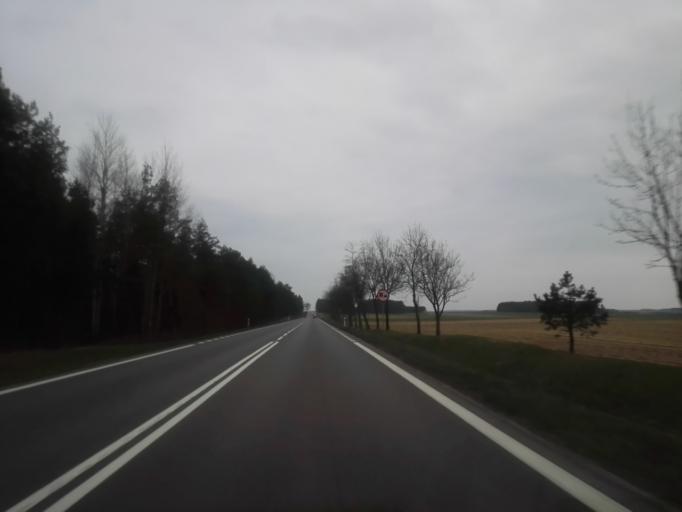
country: PL
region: Podlasie
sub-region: Powiat kolnenski
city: Stawiski
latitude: 53.4420
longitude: 22.1790
